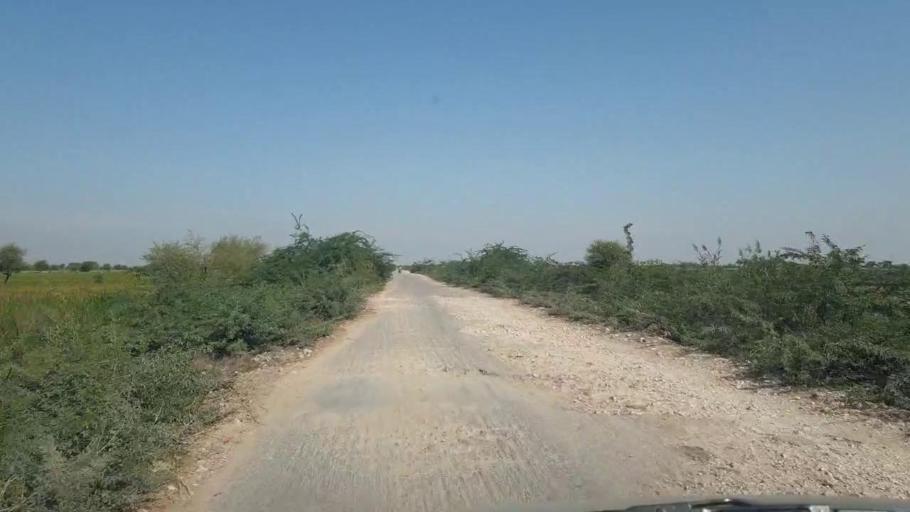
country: PK
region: Sindh
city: Tando Bago
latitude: 24.8274
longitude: 68.9880
